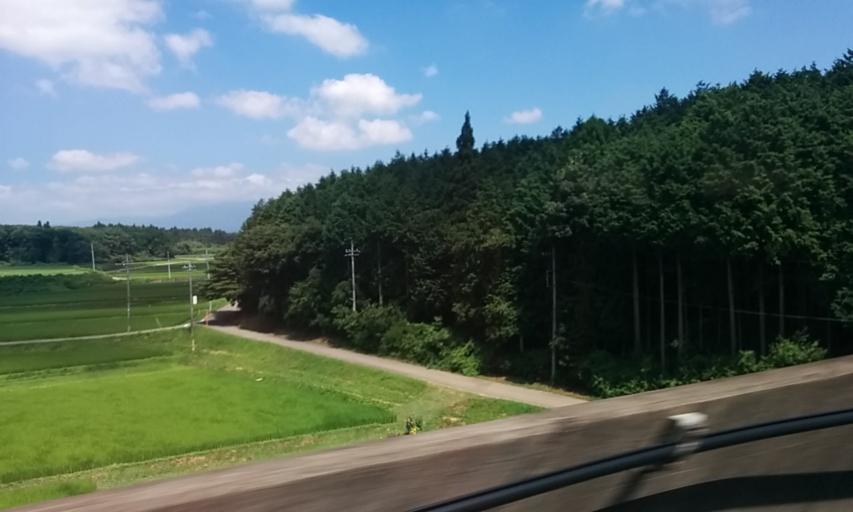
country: JP
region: Tochigi
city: Kuroiso
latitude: 36.9965
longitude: 140.0825
